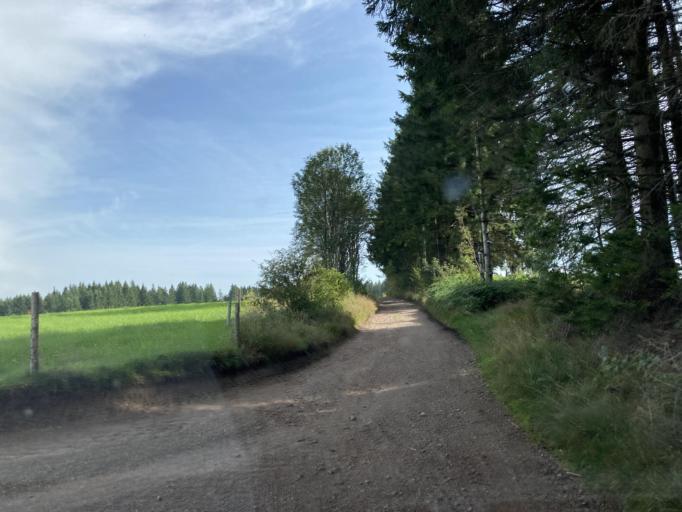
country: DE
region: Baden-Wuerttemberg
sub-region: Freiburg Region
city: Schonwald im Schwarzwald
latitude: 48.0833
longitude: 8.2354
